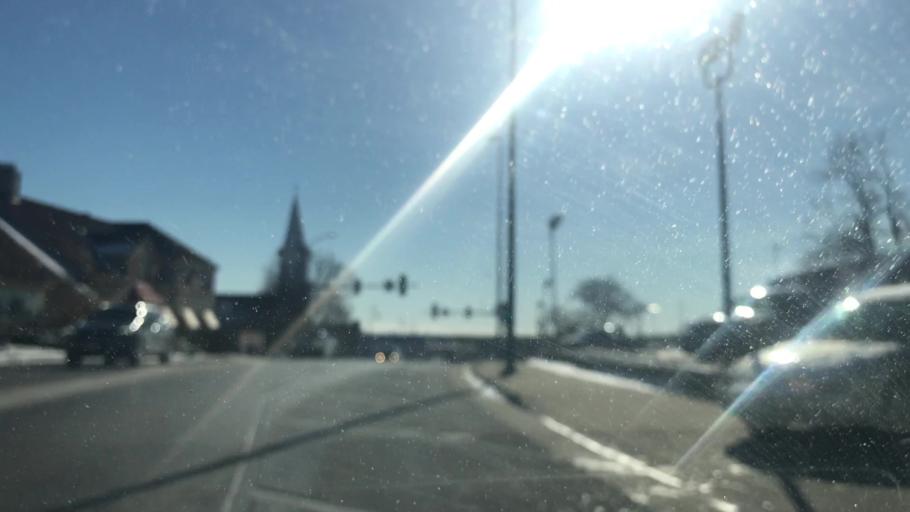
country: US
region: Wisconsin
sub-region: Waukesha County
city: Menomonee Falls
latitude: 43.1817
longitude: -88.1203
